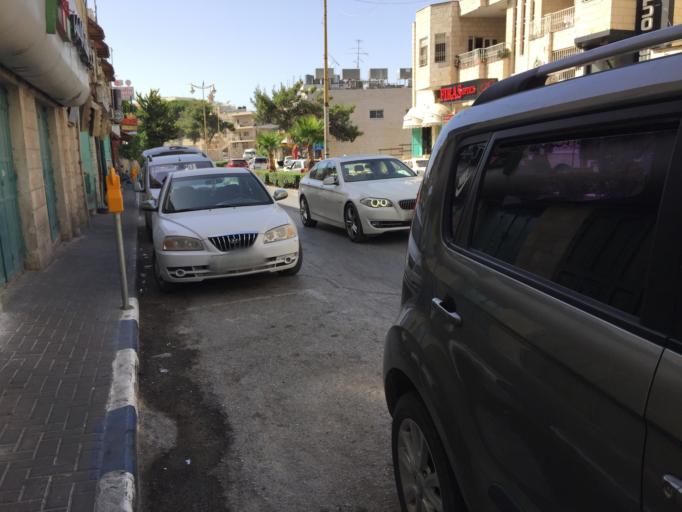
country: PS
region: West Bank
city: Bethlehem
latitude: 31.7118
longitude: 35.2030
